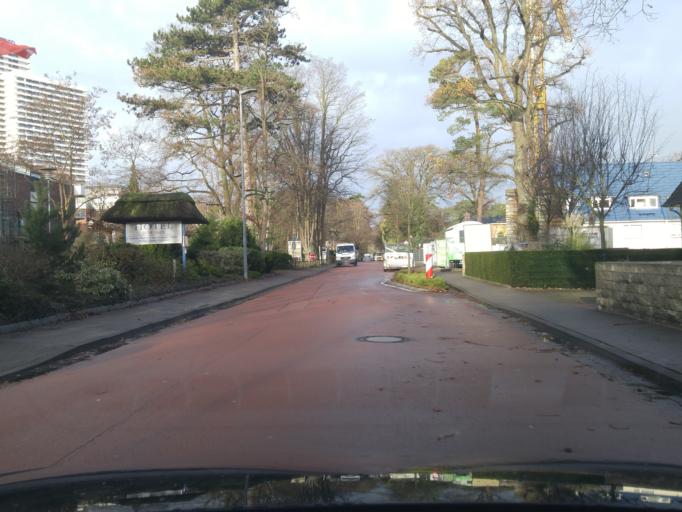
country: DE
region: Schleswig-Holstein
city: Timmendorfer Strand
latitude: 54.0041
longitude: 10.7758
